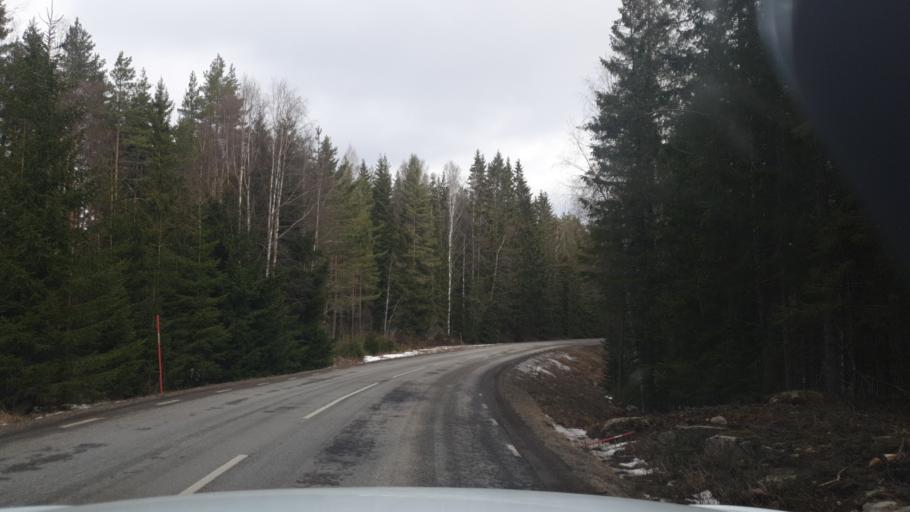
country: SE
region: Vaermland
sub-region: Eda Kommun
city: Amotfors
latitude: 59.5963
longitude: 12.2991
